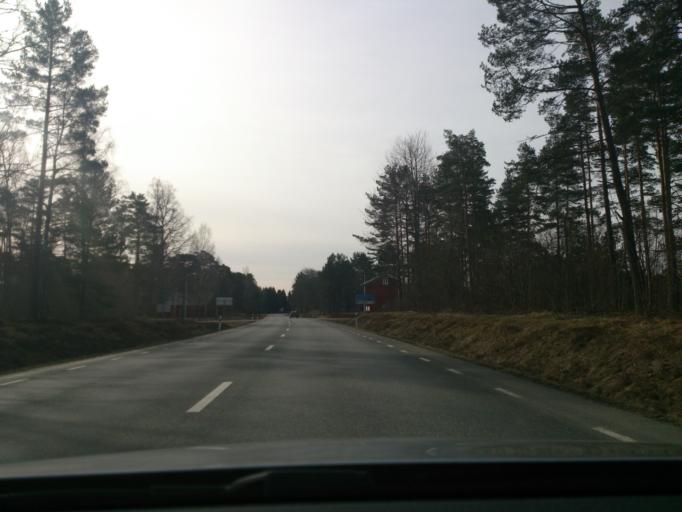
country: SE
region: Kronoberg
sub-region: Alvesta Kommun
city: Moheda
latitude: 56.9734
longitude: 14.5687
